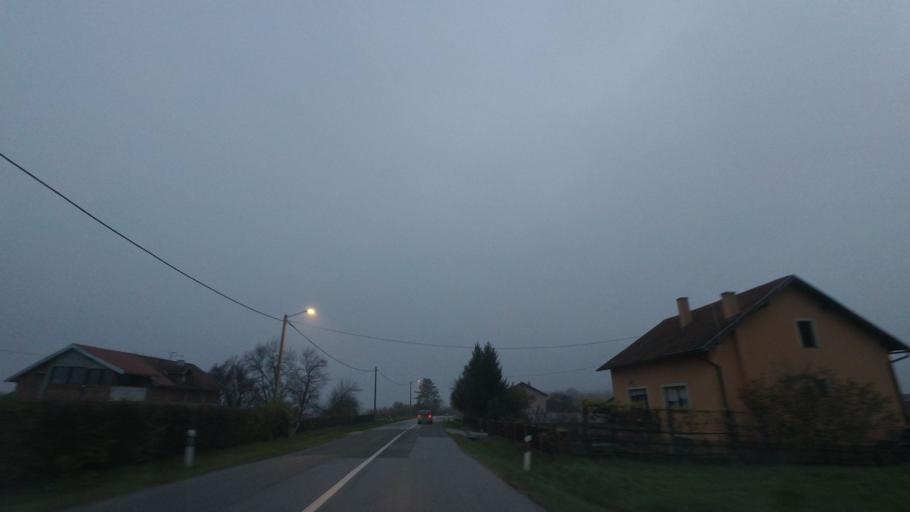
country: HR
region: Sisacko-Moslavacka
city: Glina
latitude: 45.4063
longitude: 16.1729
